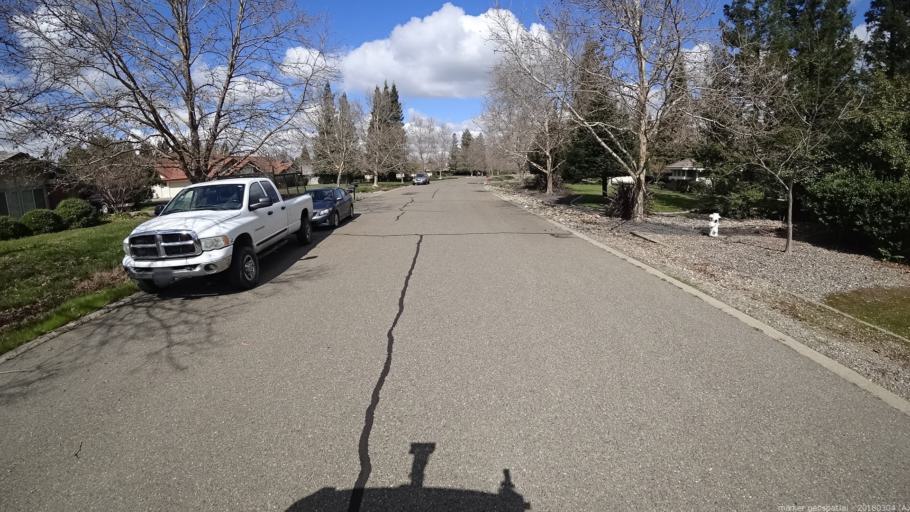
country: US
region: California
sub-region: Sacramento County
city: Vineyard
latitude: 38.4571
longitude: -121.3146
